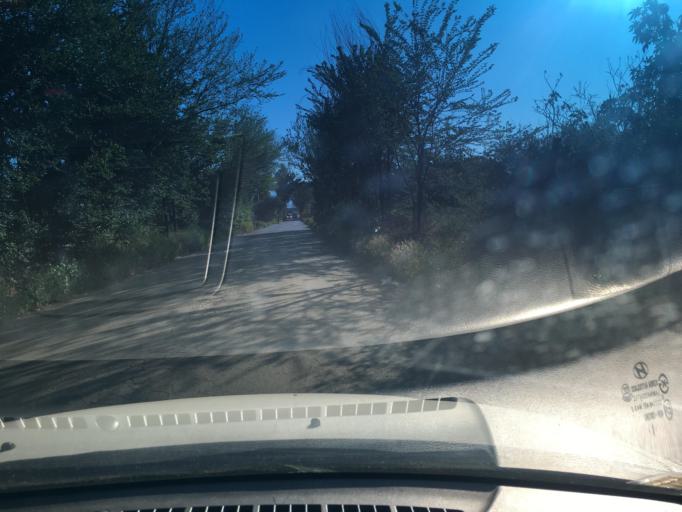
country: CL
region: Santiago Metropolitan
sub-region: Provincia de Chacabuco
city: Chicureo Abajo
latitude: -33.3122
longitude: -70.7179
